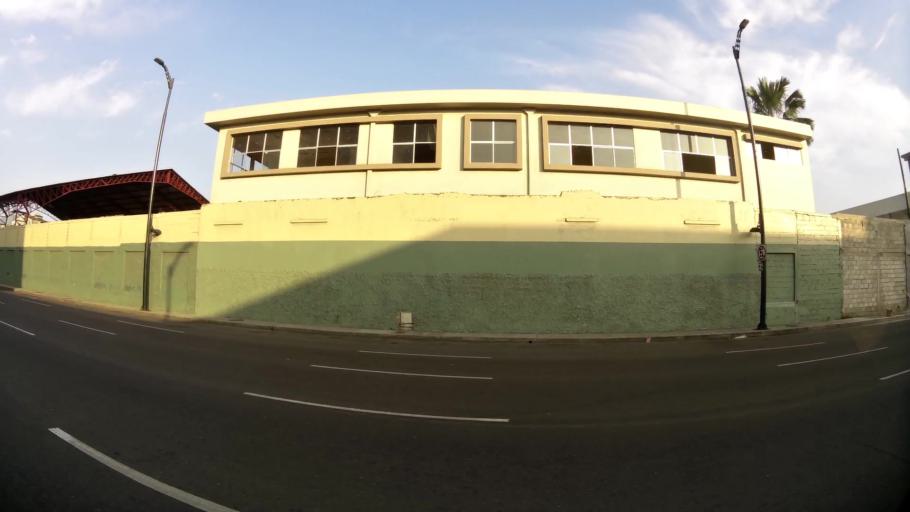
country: EC
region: Guayas
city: Guayaquil
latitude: -2.2030
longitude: -79.8937
